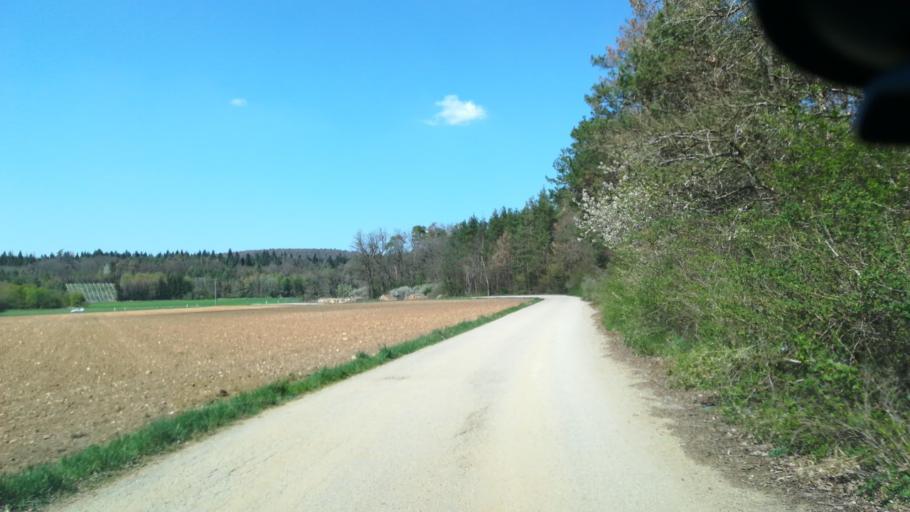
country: DE
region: Baden-Wuerttemberg
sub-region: Freiburg Region
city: Muhlhausen-Ehingen
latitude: 47.8387
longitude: 8.8177
